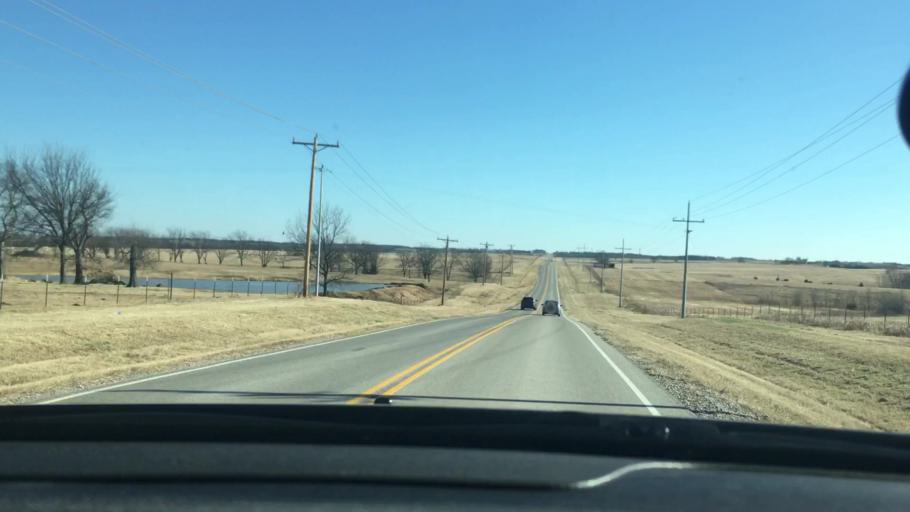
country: US
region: Oklahoma
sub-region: Murray County
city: Davis
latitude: 34.4773
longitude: -97.1033
